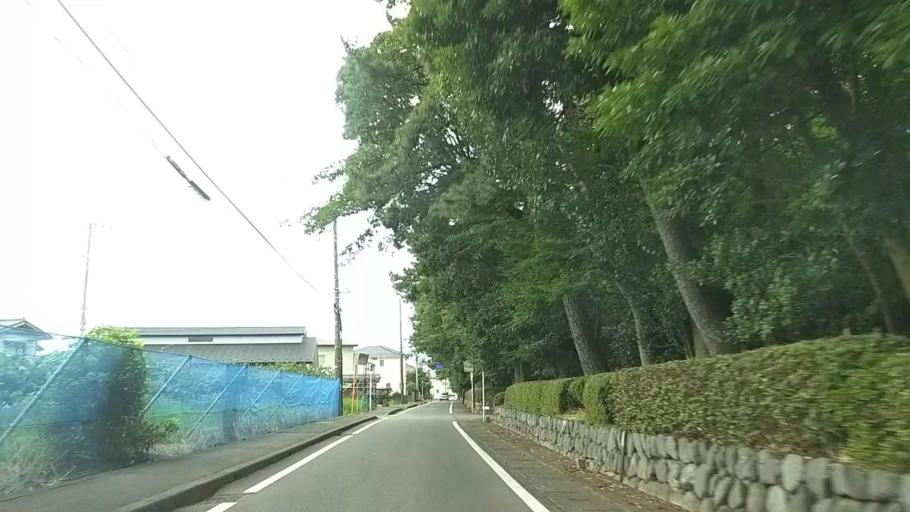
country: JP
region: Kanagawa
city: Chigasaki
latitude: 35.3723
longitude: 139.3809
